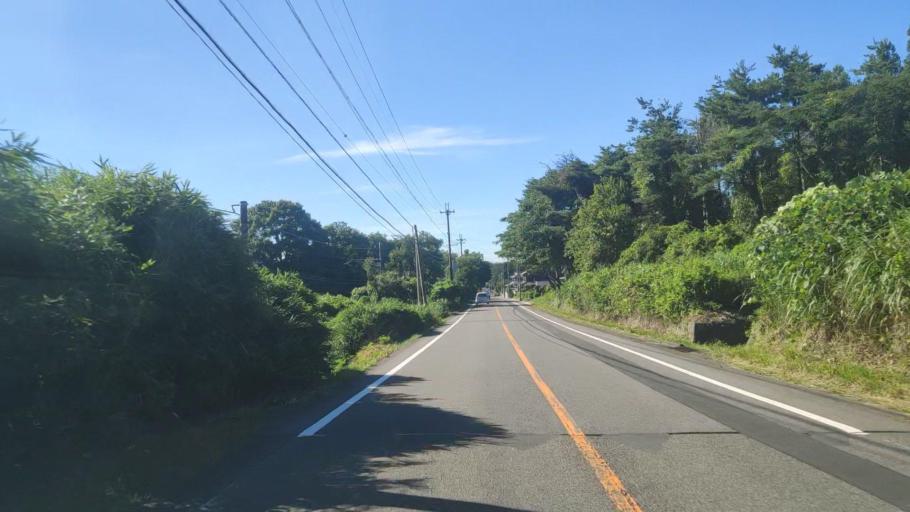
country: JP
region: Shiga Prefecture
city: Minakuchicho-matoba
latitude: 34.8713
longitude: 136.2420
